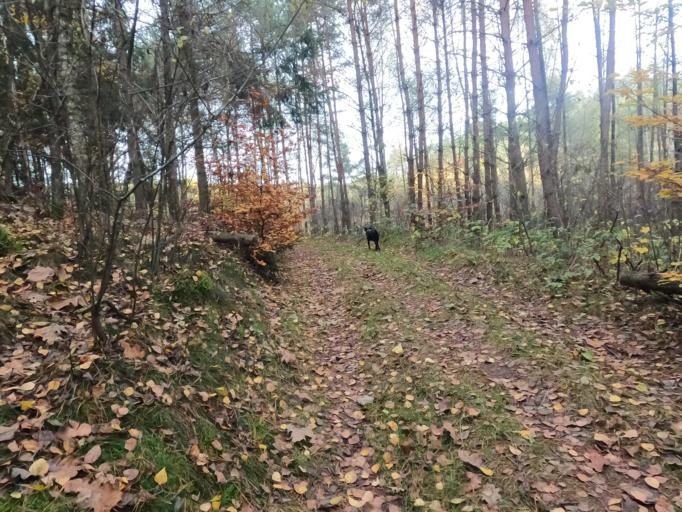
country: PL
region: Pomeranian Voivodeship
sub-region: Powiat starogardzki
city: Skarszewy
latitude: 54.0077
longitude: 18.4603
